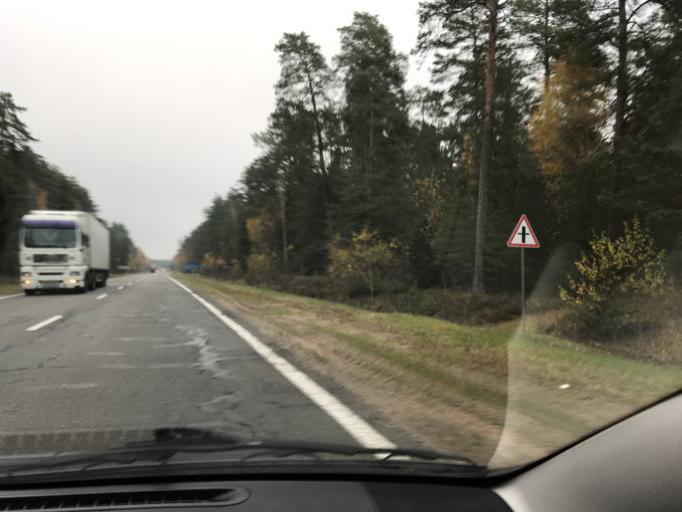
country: BY
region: Vitebsk
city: Syanno
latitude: 55.0531
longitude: 29.5213
